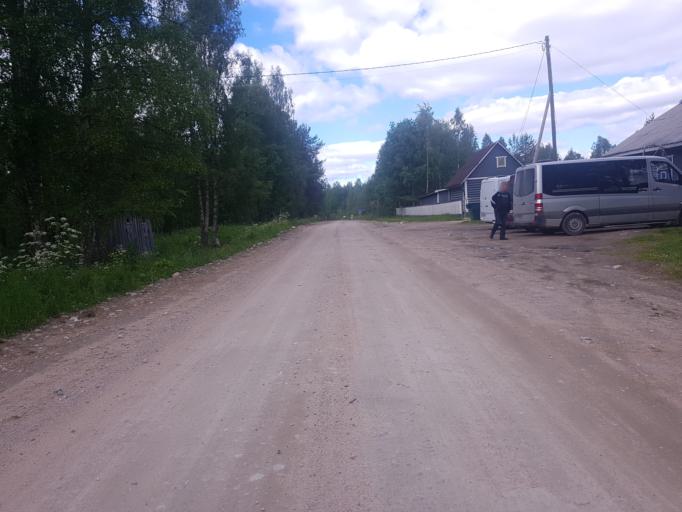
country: RU
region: Republic of Karelia
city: Kostomuksha
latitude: 65.1861
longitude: 30.2883
